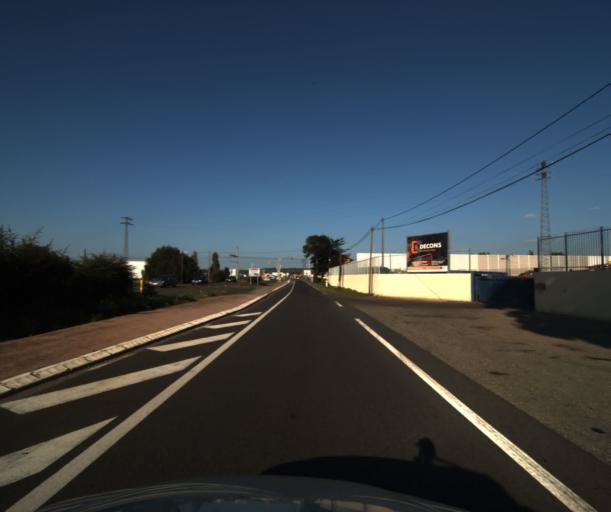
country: FR
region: Midi-Pyrenees
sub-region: Departement de la Haute-Garonne
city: Pinsaguel
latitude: 43.5174
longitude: 1.3834
